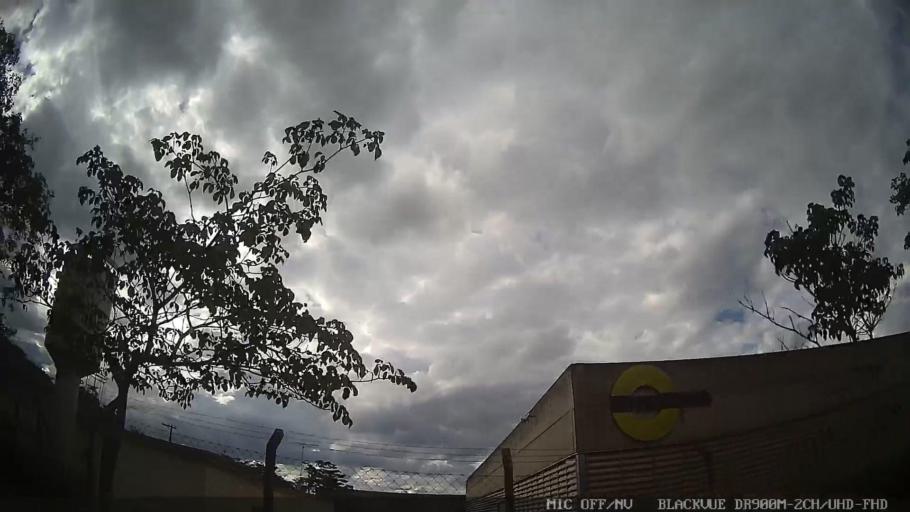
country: BR
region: Sao Paulo
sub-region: Jaguariuna
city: Jaguariuna
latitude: -22.6889
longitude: -47.0014
